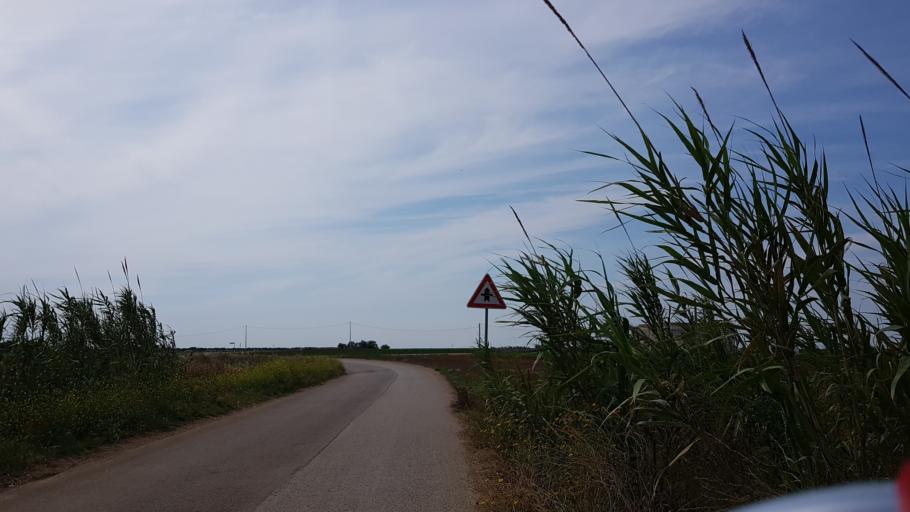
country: IT
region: Apulia
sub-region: Provincia di Brindisi
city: San Vito dei Normanni
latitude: 40.6659
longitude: 17.8140
